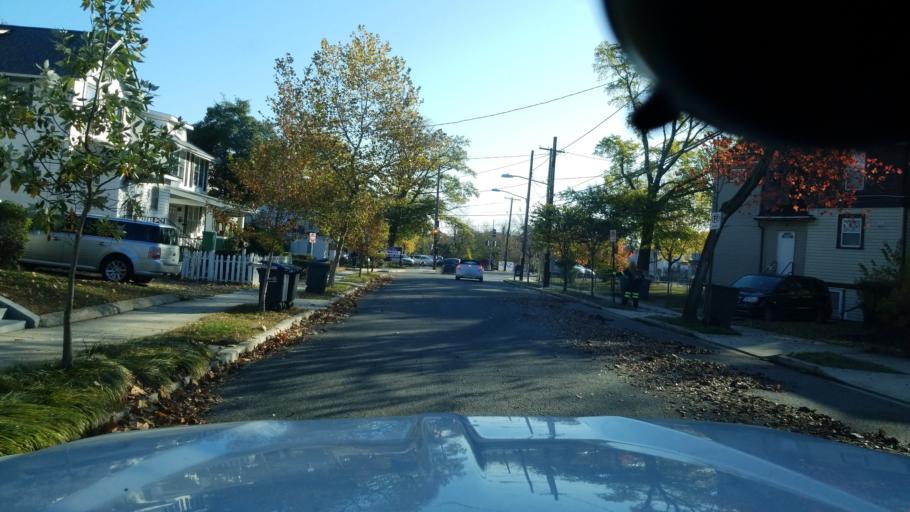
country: US
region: Maryland
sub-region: Prince George's County
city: Mount Rainier
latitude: 38.9331
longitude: -76.9689
